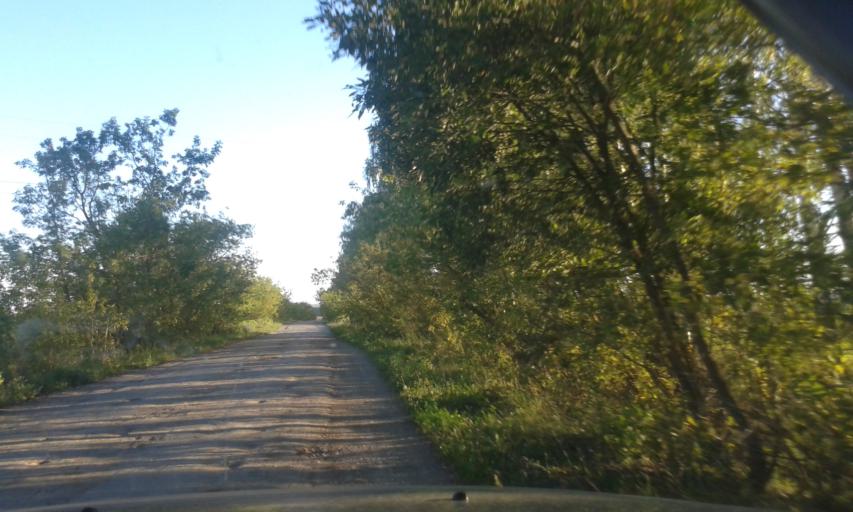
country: RU
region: Tula
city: Krapivna
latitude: 54.1293
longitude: 37.1564
